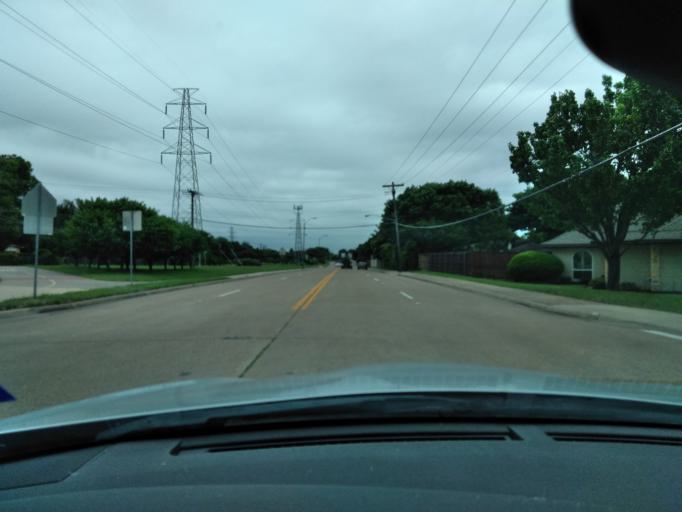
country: US
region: Texas
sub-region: Dallas County
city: Richardson
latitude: 32.9540
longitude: -96.7787
